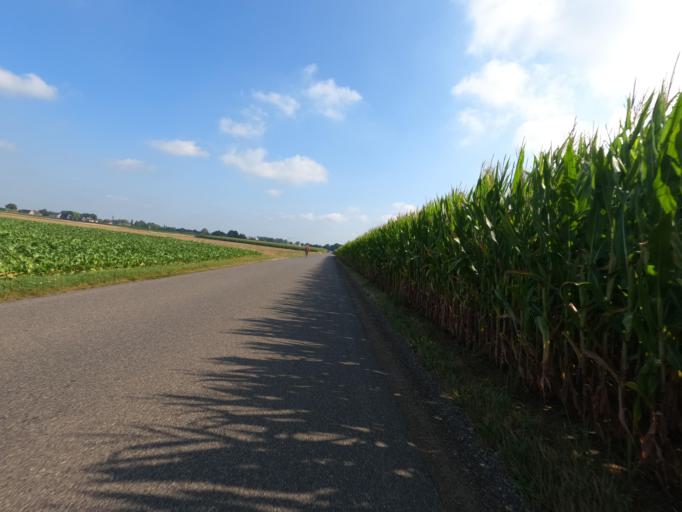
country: DE
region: North Rhine-Westphalia
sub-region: Regierungsbezirk Koln
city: Heinsberg
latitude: 51.0861
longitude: 6.0860
